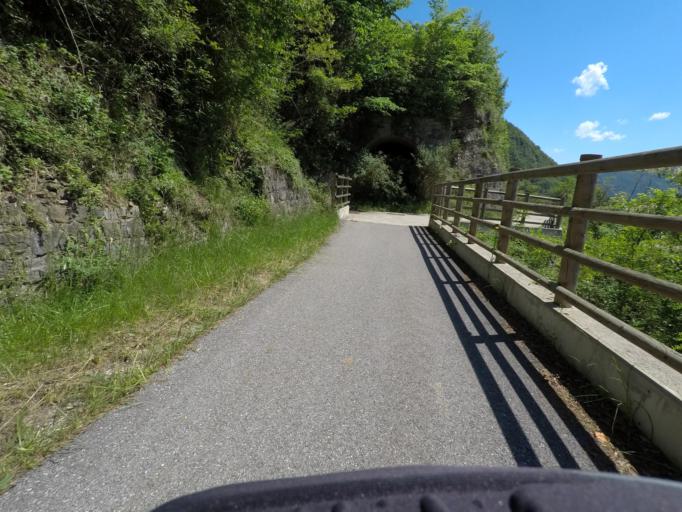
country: IT
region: Friuli Venezia Giulia
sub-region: Provincia di Udine
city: Raveo
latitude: 46.4297
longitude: 12.8976
